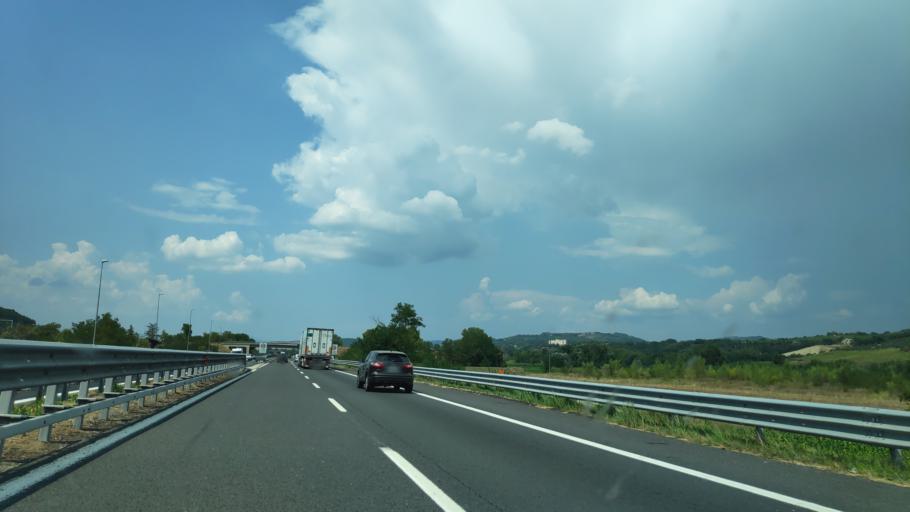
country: IT
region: Umbria
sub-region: Provincia di Terni
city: Orvieto Scalo
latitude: 42.7115
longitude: 12.1536
